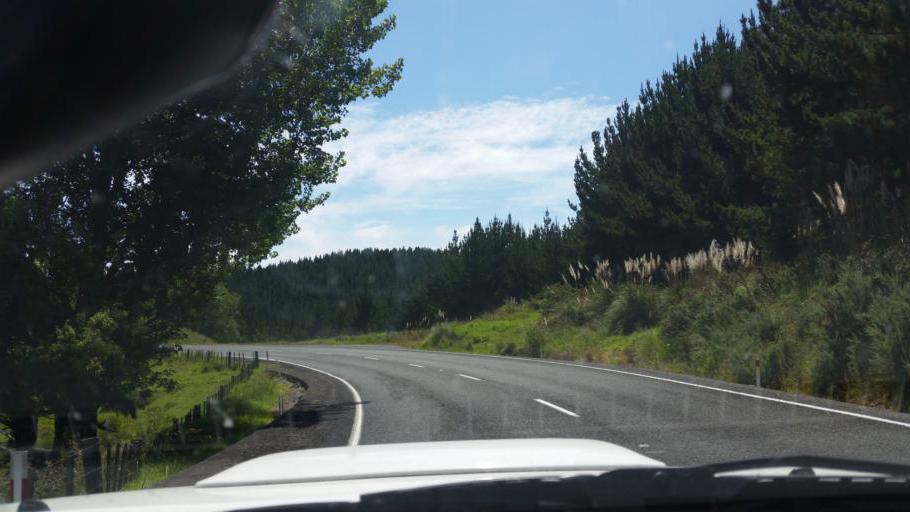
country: NZ
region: Auckland
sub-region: Auckland
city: Wellsford
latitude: -36.2034
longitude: 174.3958
